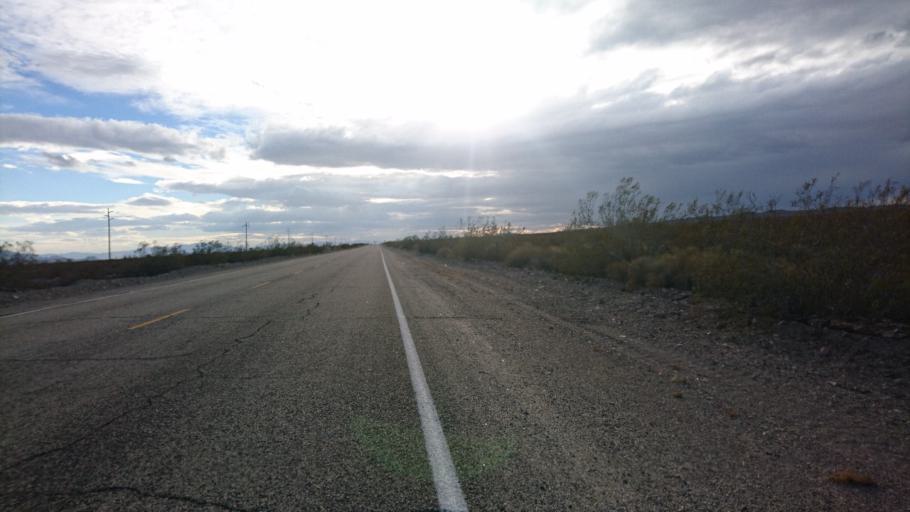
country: US
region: California
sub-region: San Bernardino County
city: Needles
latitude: 34.6713
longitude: -115.3390
